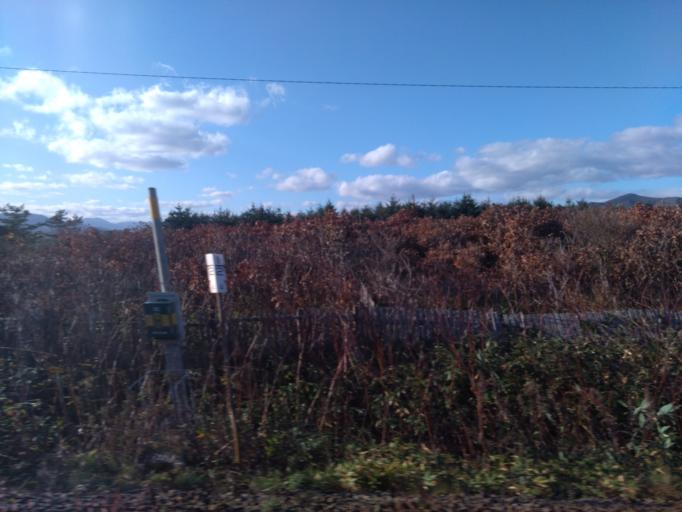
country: JP
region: Hokkaido
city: Niseko Town
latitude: 42.5439
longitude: 140.4101
